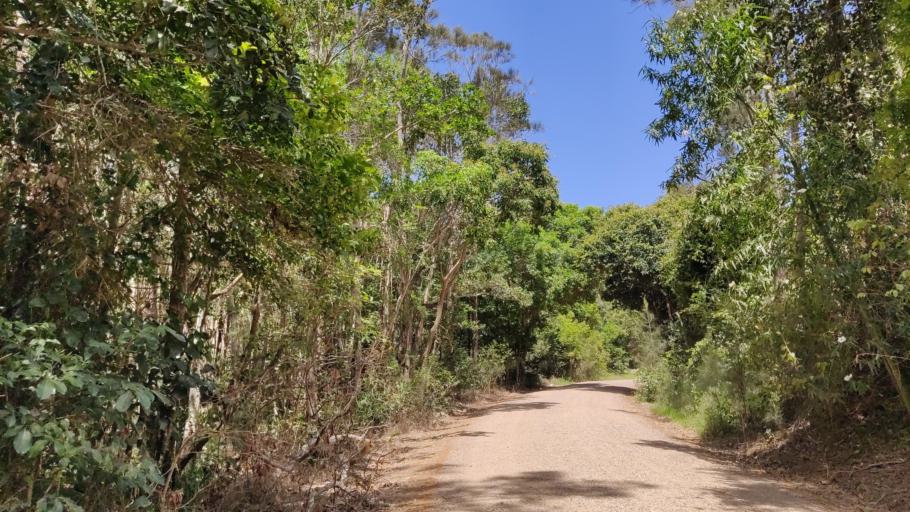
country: AU
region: New South Wales
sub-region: Port Macquarie-Hastings
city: North Haven
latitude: -31.6396
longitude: 152.8315
